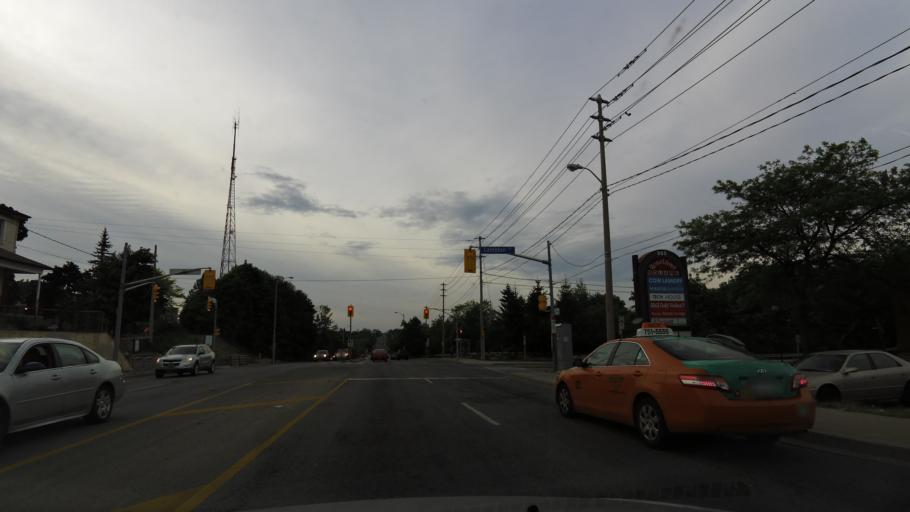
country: CA
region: Ontario
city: Etobicoke
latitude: 43.6807
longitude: -79.4976
